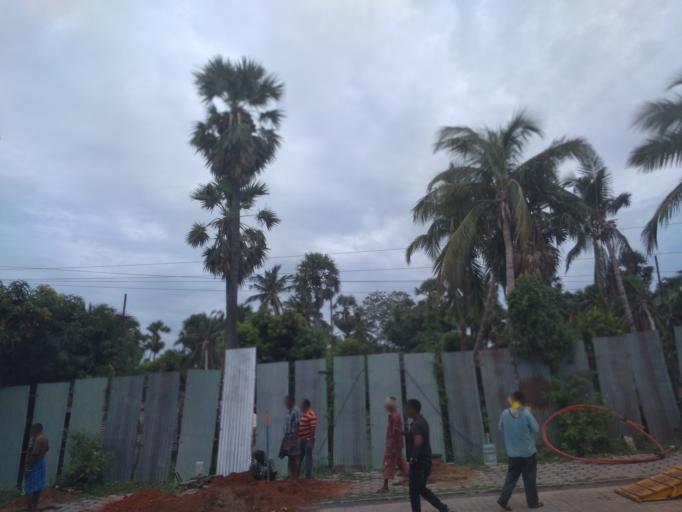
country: IN
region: Tamil Nadu
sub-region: Kancheepuram
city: Injambakkam
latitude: 12.8571
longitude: 80.2264
